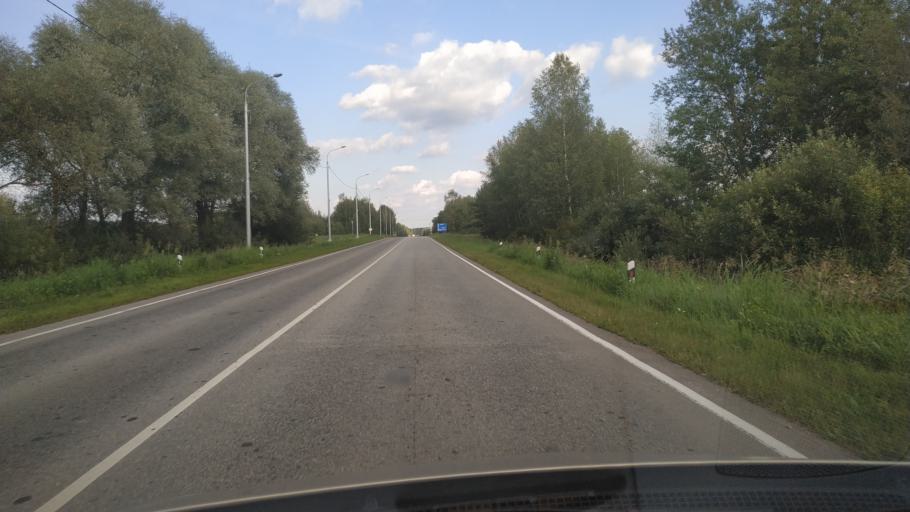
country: RU
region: Moskovskaya
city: Vereya
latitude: 55.7079
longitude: 39.1194
